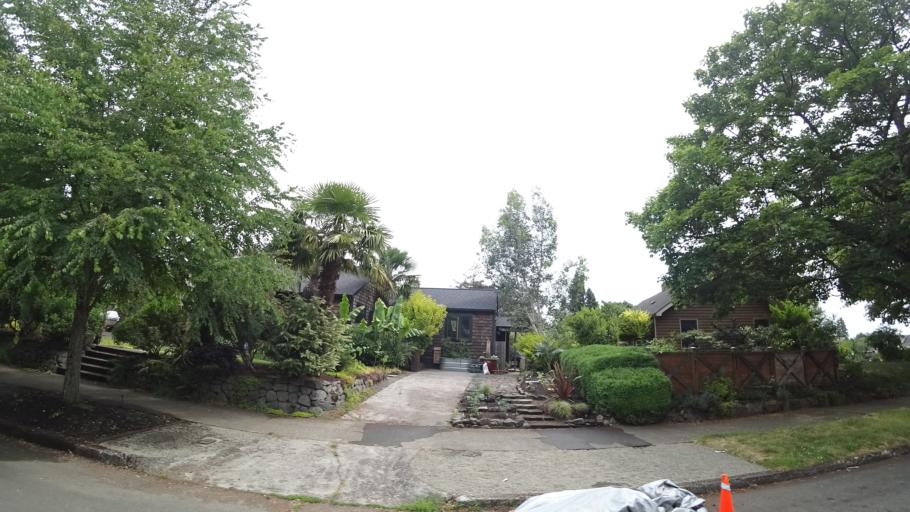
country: US
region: Oregon
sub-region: Multnomah County
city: Portland
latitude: 45.5657
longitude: -122.6991
